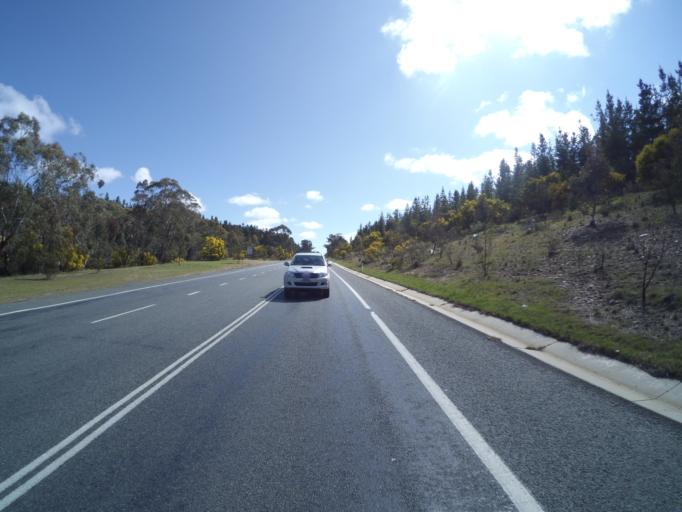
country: AU
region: New South Wales
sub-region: Queanbeyan
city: Queanbeyan
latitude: -35.2662
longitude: 149.2635
